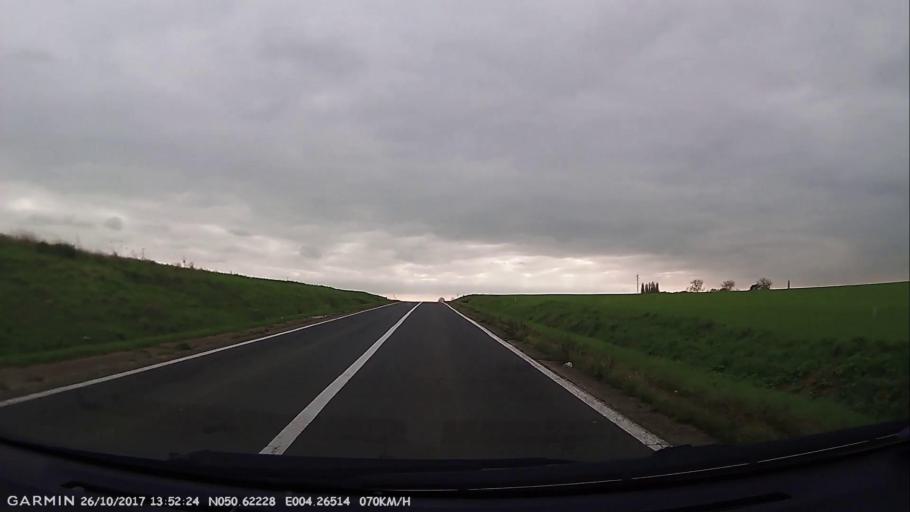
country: BE
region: Wallonia
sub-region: Province du Brabant Wallon
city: Ittre
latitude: 50.6221
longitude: 4.2651
